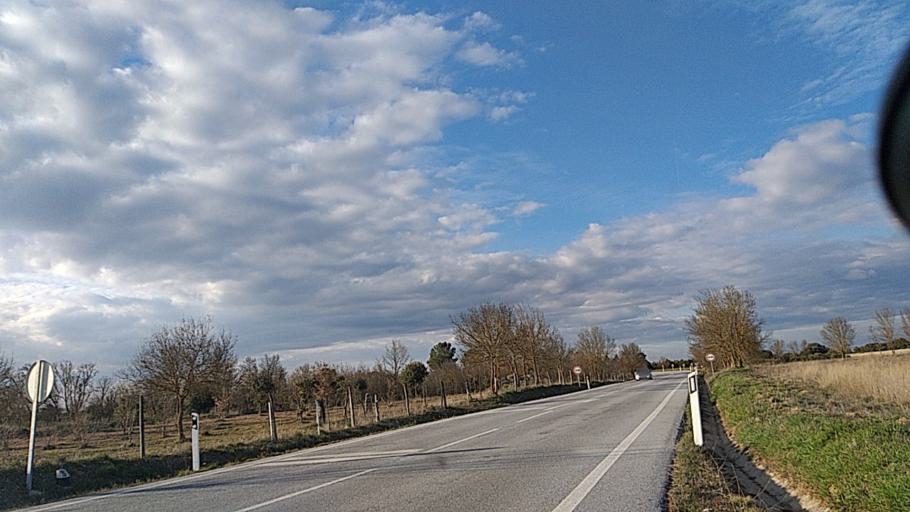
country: ES
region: Castille and Leon
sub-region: Provincia de Salamanca
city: Aldea del Obispo
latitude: 40.6799
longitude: -6.8683
